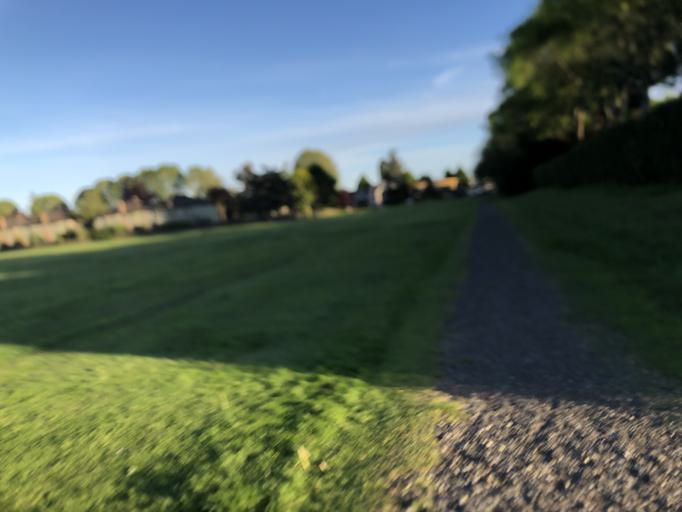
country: CA
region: British Columbia
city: Richmond
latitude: 49.1454
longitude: -123.1337
